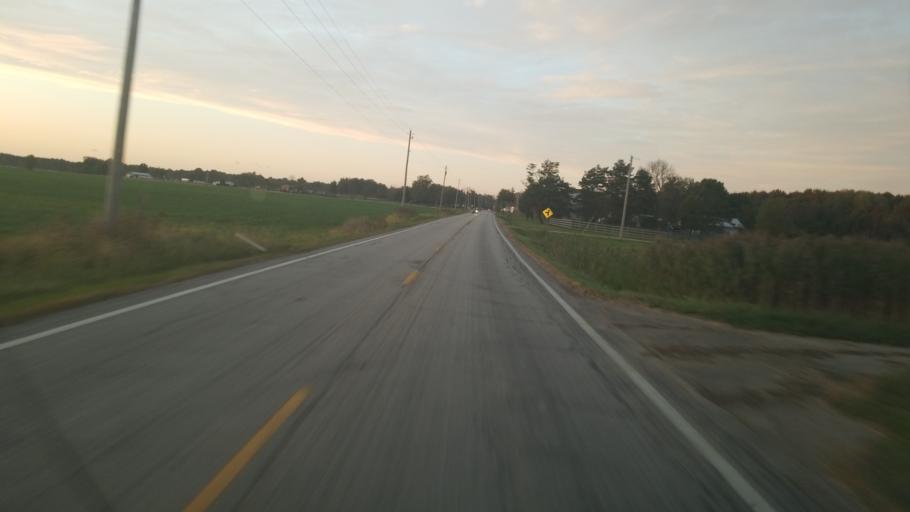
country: US
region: Ohio
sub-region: Ashtabula County
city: Andover
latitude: 41.6689
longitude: -80.6676
